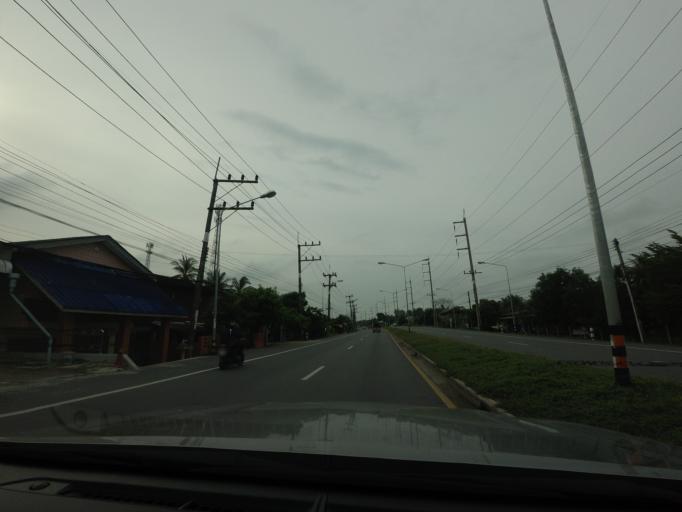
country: TH
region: Songkhla
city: Krasae Sin
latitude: 7.6499
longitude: 100.3883
